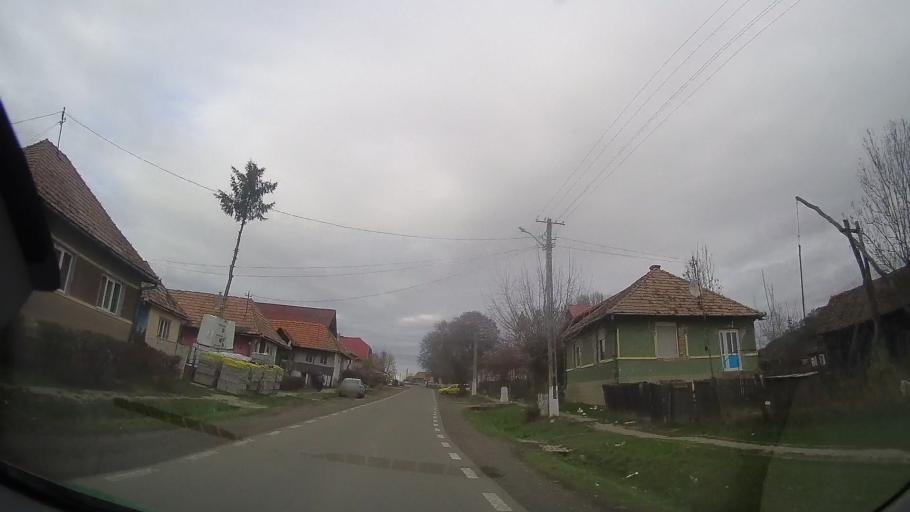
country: RO
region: Mures
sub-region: Comuna Faragau
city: Faragau
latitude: 46.7794
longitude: 24.5530
